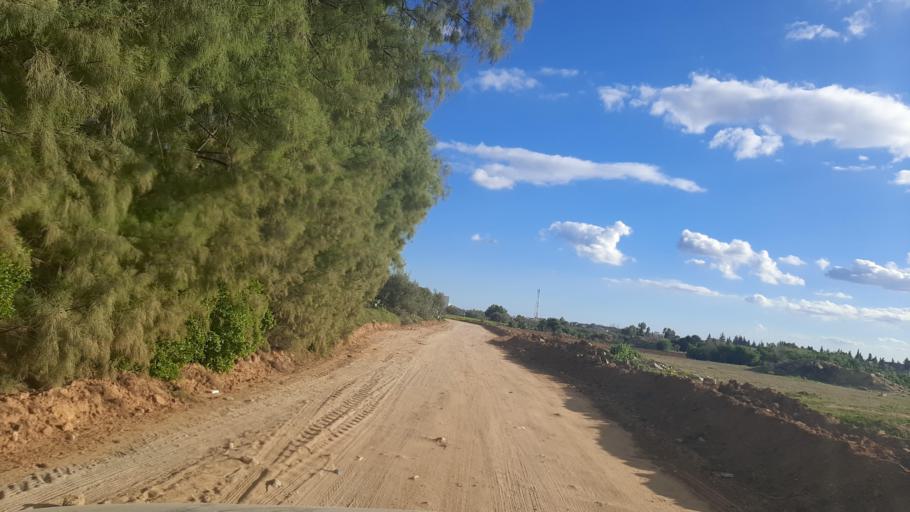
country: TN
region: Nabul
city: Al Hammamat
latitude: 36.4230
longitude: 10.5083
